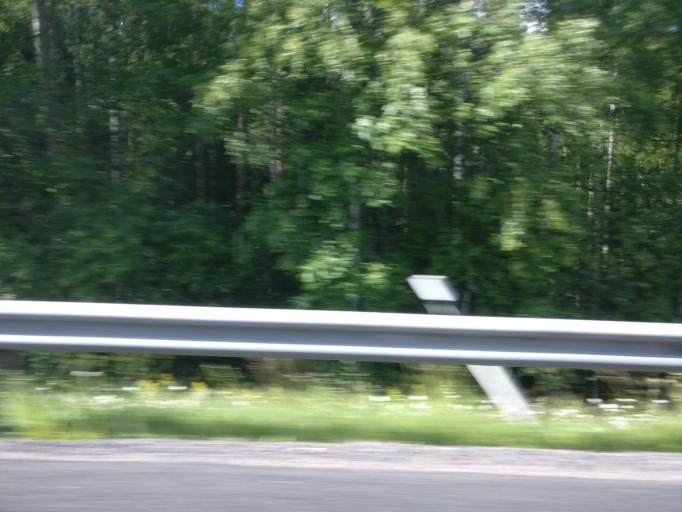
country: FI
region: Uusimaa
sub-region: Helsinki
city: Jaervenpaeae
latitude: 60.6176
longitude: 25.0322
